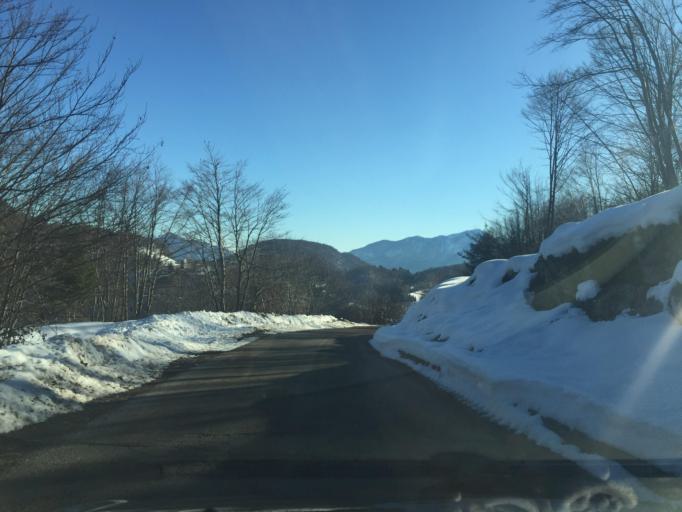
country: IT
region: Friuli Venezia Giulia
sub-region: Provincia di Udine
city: Lauco
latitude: 46.4384
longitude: 12.9633
